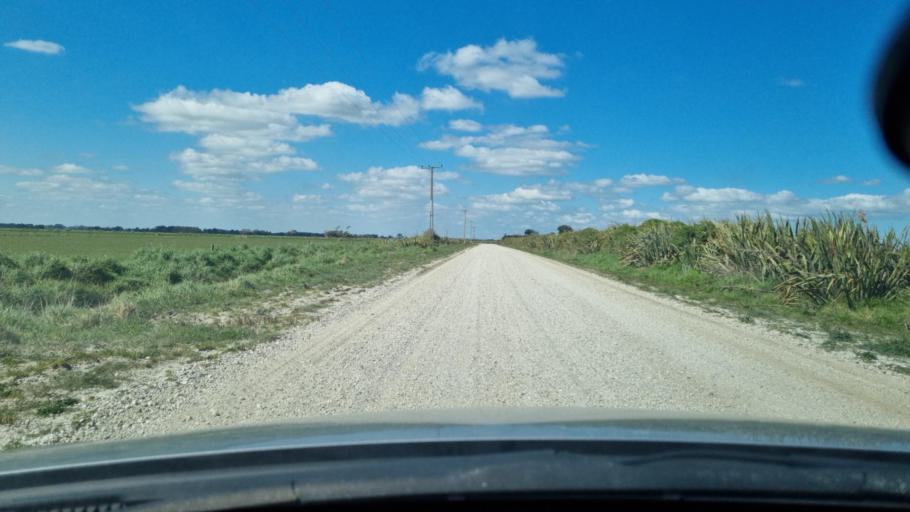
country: NZ
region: Southland
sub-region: Invercargill City
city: Invercargill
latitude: -46.3933
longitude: 168.2421
